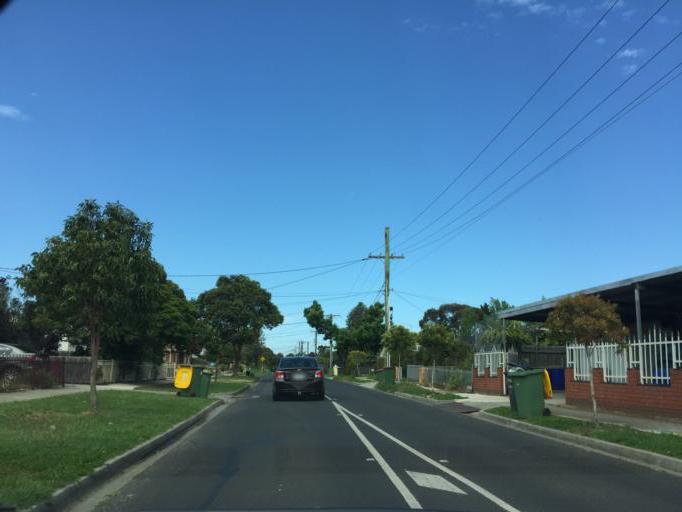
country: AU
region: Victoria
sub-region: Maribyrnong
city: Braybrook
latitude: -37.7820
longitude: 144.8569
